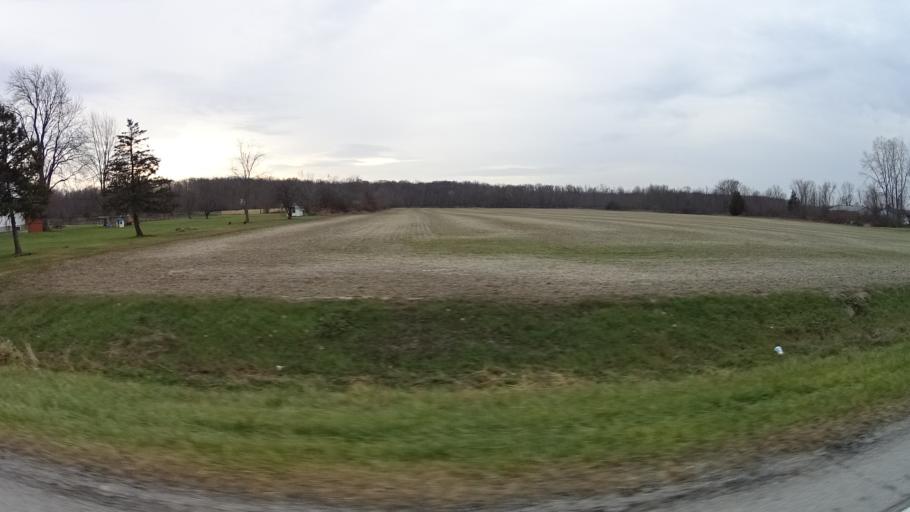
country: US
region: Ohio
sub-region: Lorain County
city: Lagrange
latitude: 41.1688
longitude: -82.1433
